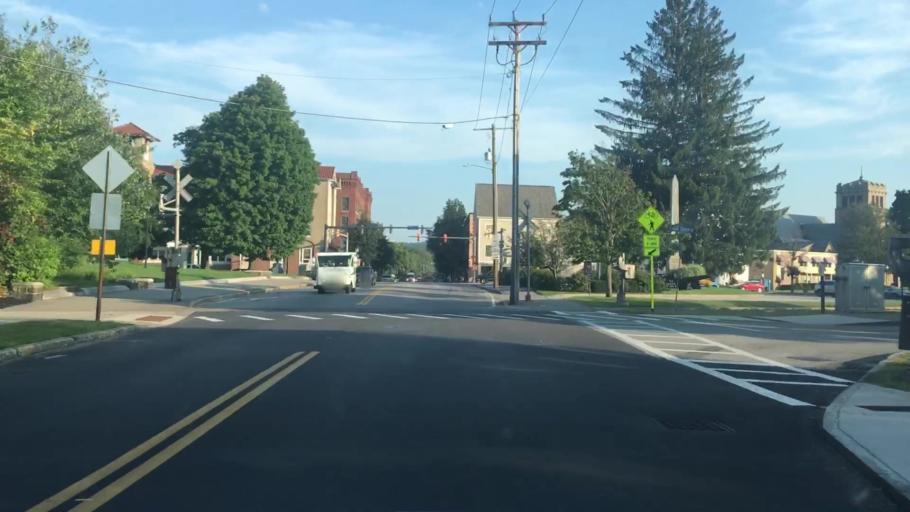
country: US
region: New Hampshire
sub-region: Belknap County
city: Laconia
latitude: 43.5302
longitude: -71.4717
